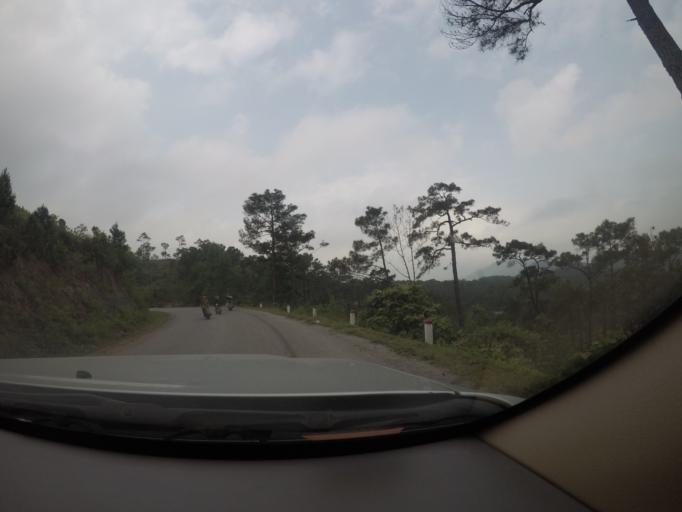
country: VN
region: Quang Binh
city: Ba Don
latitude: 17.6800
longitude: 106.4235
